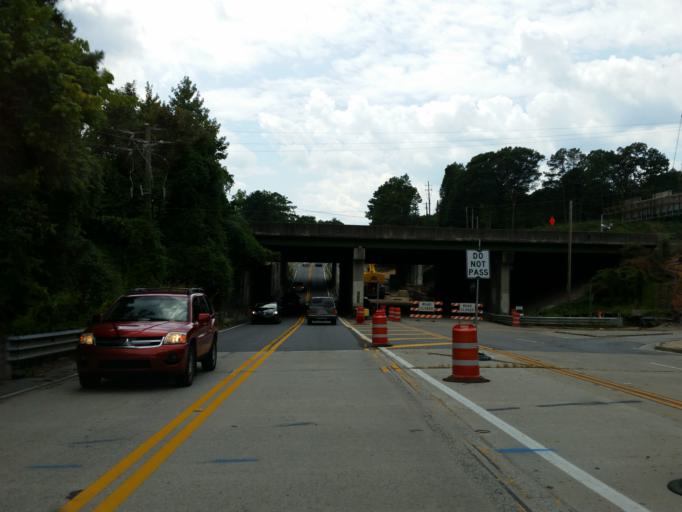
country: US
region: Georgia
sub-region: Cobb County
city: Smyrna
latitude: 33.9121
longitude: -84.4781
